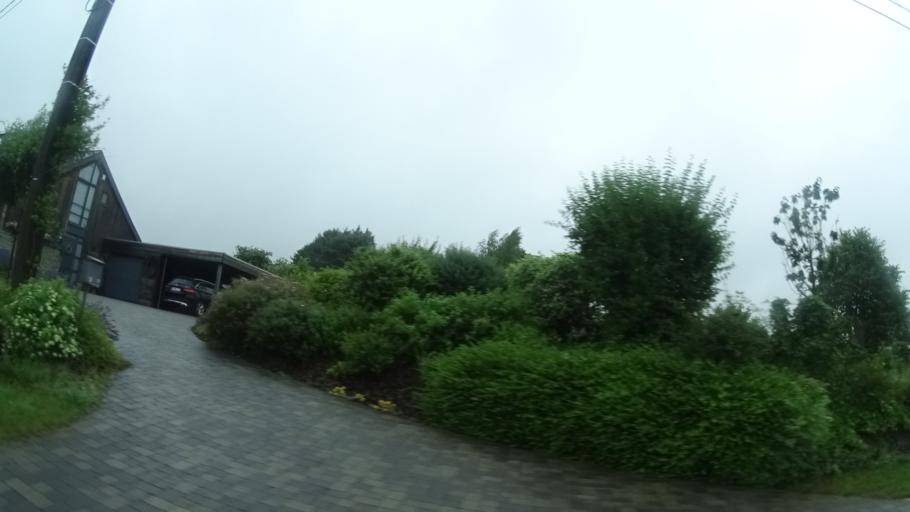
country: BE
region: Wallonia
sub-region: Province du Luxembourg
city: Paliseul
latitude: 49.8868
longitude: 5.1697
